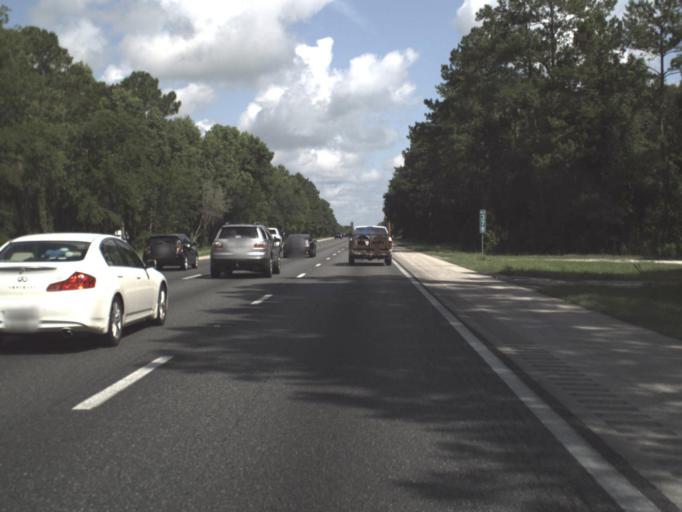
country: US
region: Florida
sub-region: Alachua County
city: Gainesville
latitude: 29.5462
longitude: -82.3344
